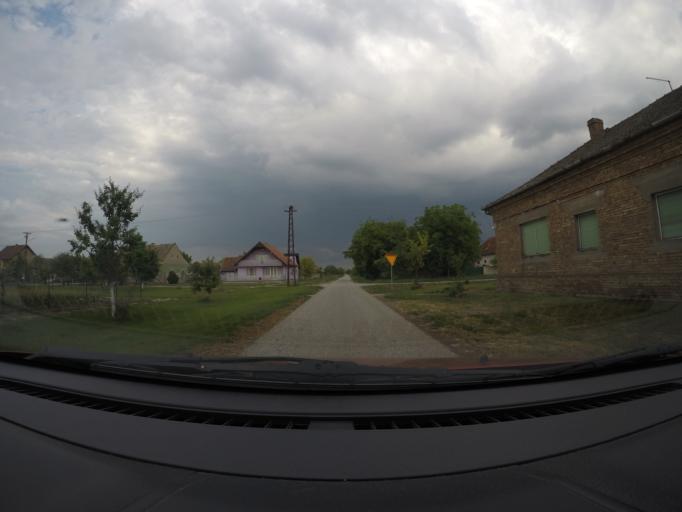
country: RS
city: Uzdin
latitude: 45.2019
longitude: 20.6178
